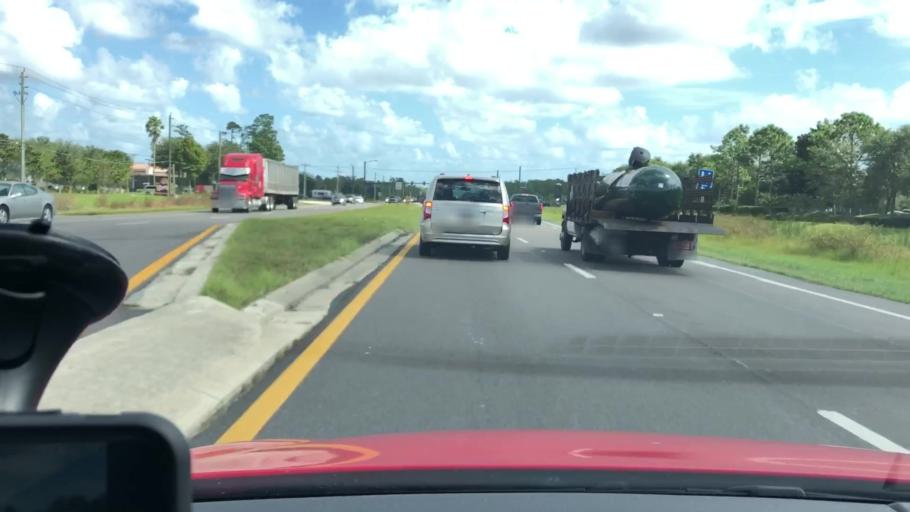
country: US
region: Florida
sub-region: Volusia County
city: Holly Hill
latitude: 29.2229
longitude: -81.0962
